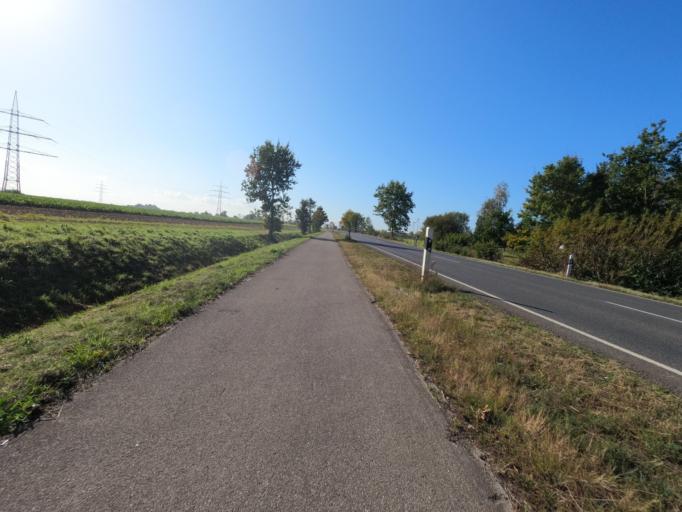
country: DE
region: North Rhine-Westphalia
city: Niedermerz
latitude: 50.8808
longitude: 6.2714
